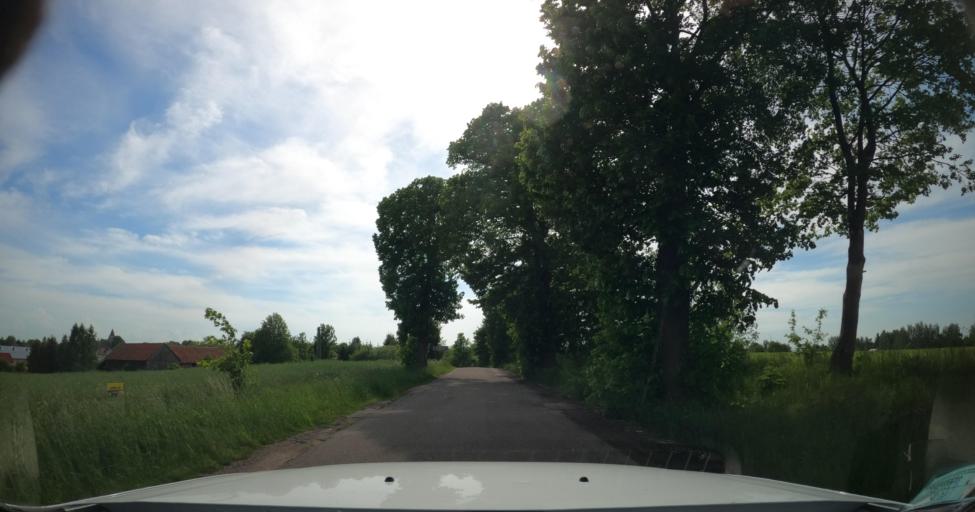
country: PL
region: Warmian-Masurian Voivodeship
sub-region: Powiat lidzbarski
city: Lubomino
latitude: 54.0734
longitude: 20.2413
